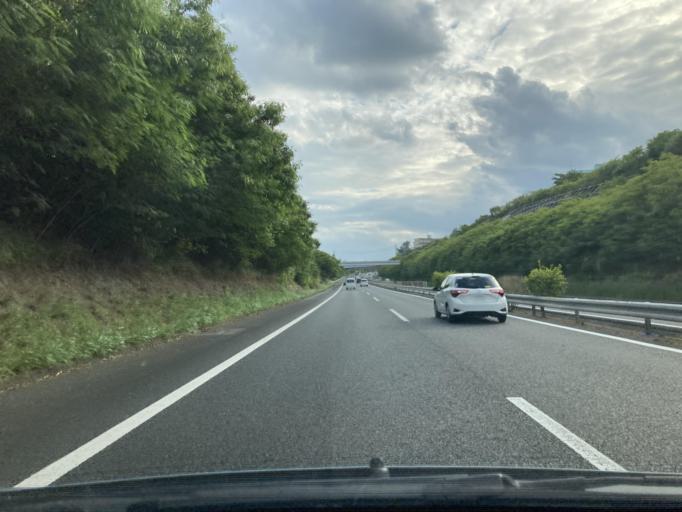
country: JP
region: Okinawa
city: Ginowan
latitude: 26.2680
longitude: 127.7748
